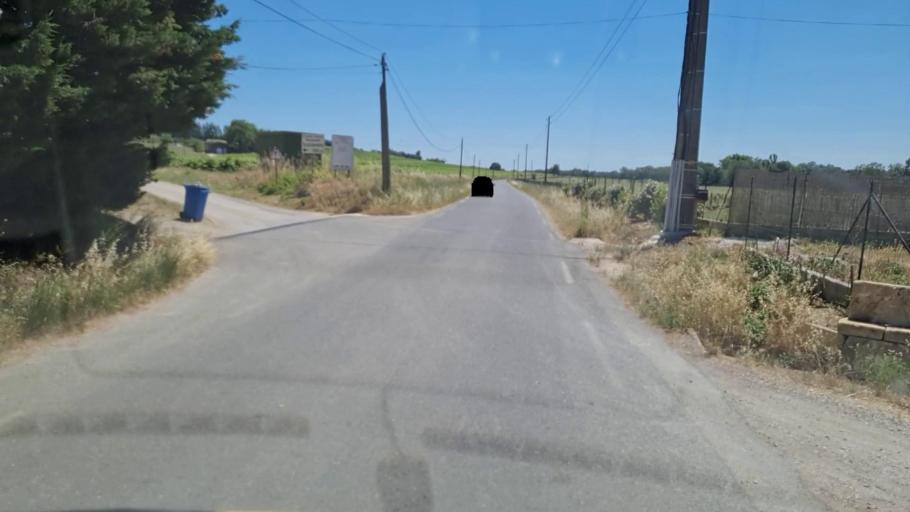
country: FR
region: Languedoc-Roussillon
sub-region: Departement du Gard
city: Le Cailar
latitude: 43.6590
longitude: 4.2563
